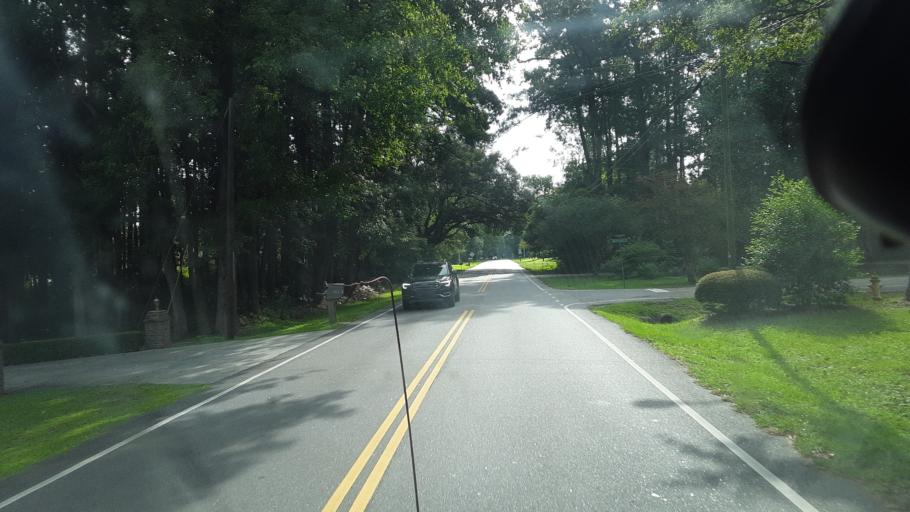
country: US
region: South Carolina
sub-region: Horry County
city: Conway
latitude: 33.8230
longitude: -79.0798
